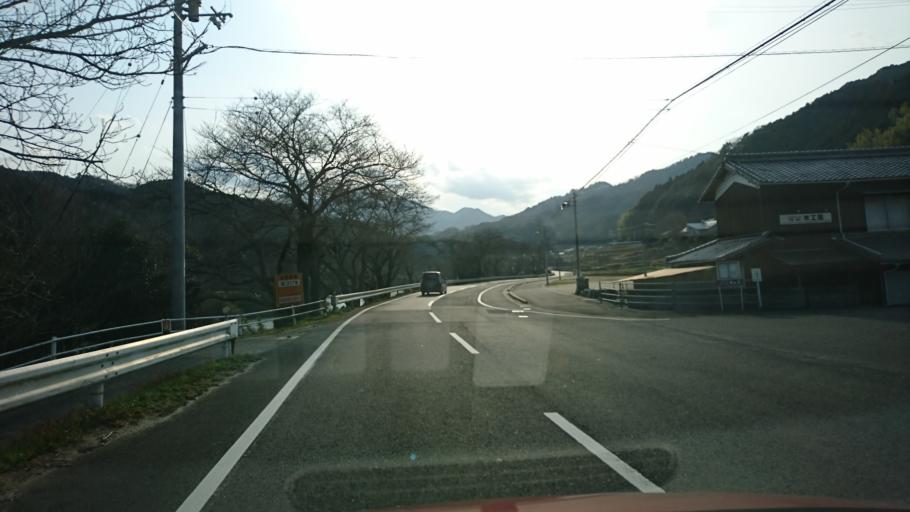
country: JP
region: Ehime
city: Hojo
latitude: 33.9922
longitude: 132.9143
